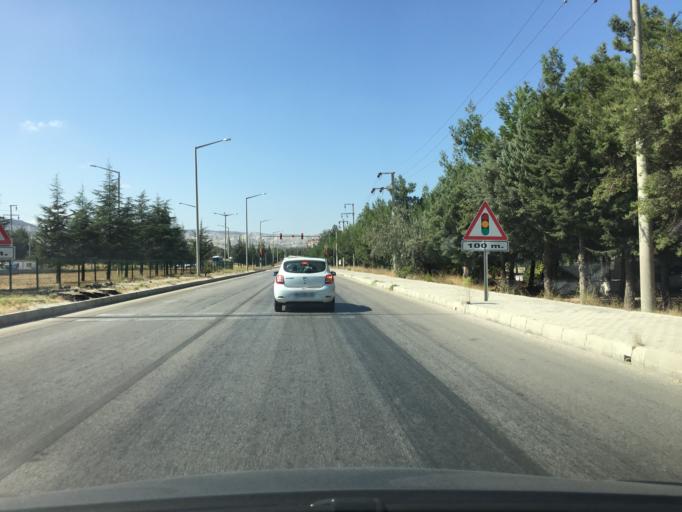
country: TR
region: Burdur
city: Burdur
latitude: 37.7308
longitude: 30.3064
